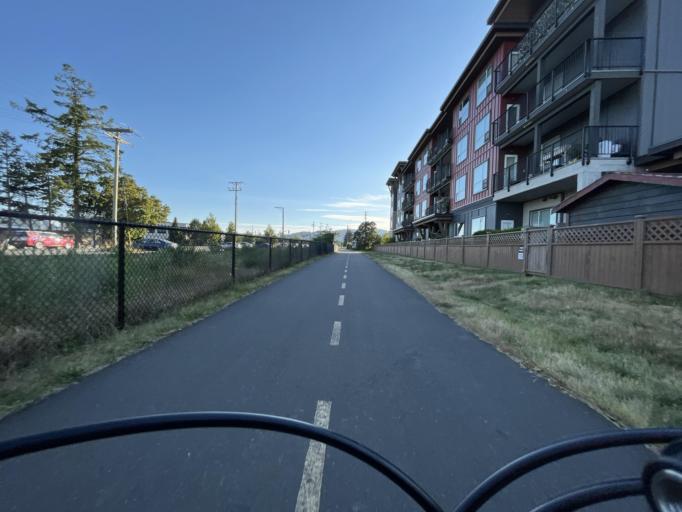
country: CA
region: British Columbia
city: Langford
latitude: 48.4452
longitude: -123.5075
